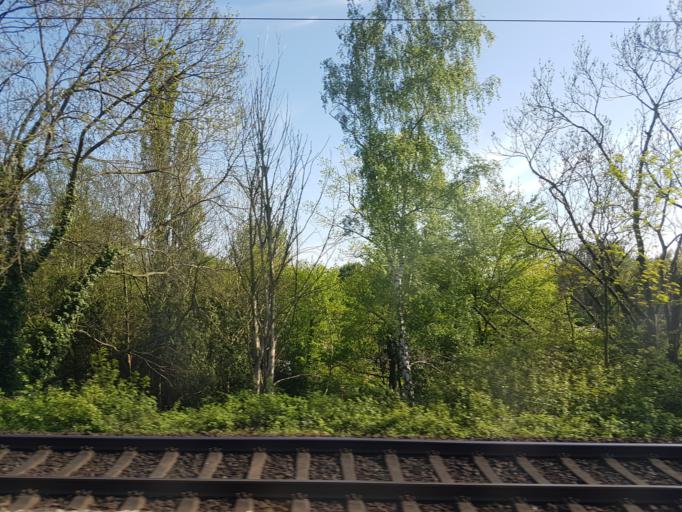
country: DE
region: Lower Saxony
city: Hannover
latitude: 52.3420
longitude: 9.7541
